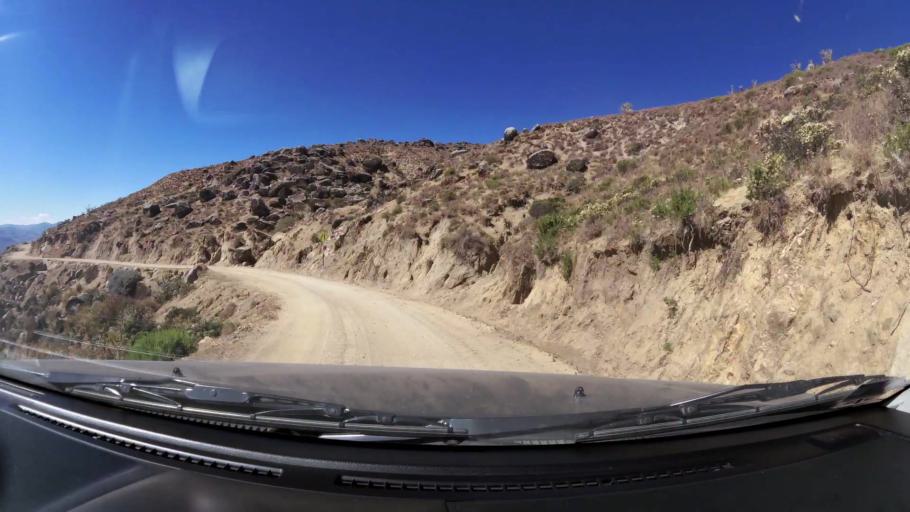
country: PE
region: Huancavelica
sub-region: Huaytara
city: Quito-Arma
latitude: -13.6264
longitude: -75.3557
